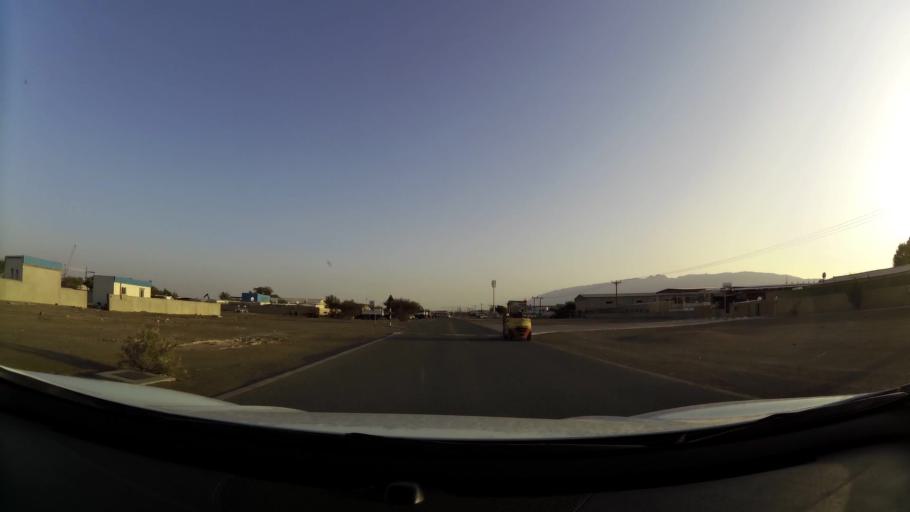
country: AE
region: Abu Dhabi
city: Al Ain
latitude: 24.1475
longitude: 55.8197
